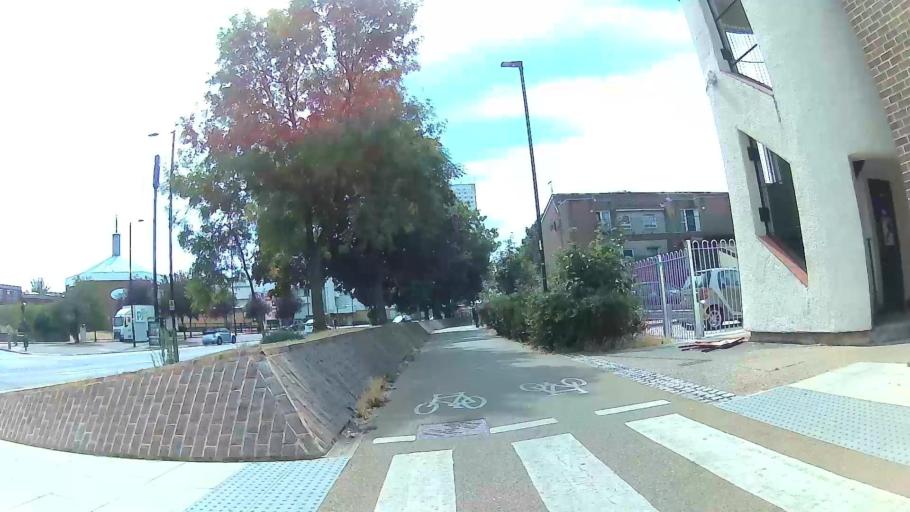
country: GB
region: England
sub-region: Greater London
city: Enfield
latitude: 51.6273
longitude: -0.0569
